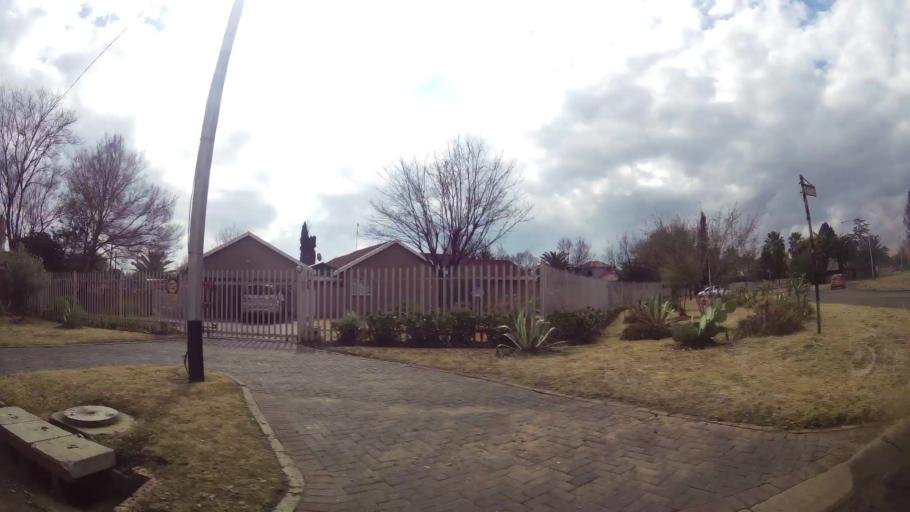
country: ZA
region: Gauteng
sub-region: Sedibeng District Municipality
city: Vereeniging
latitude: -26.6548
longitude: 27.9808
